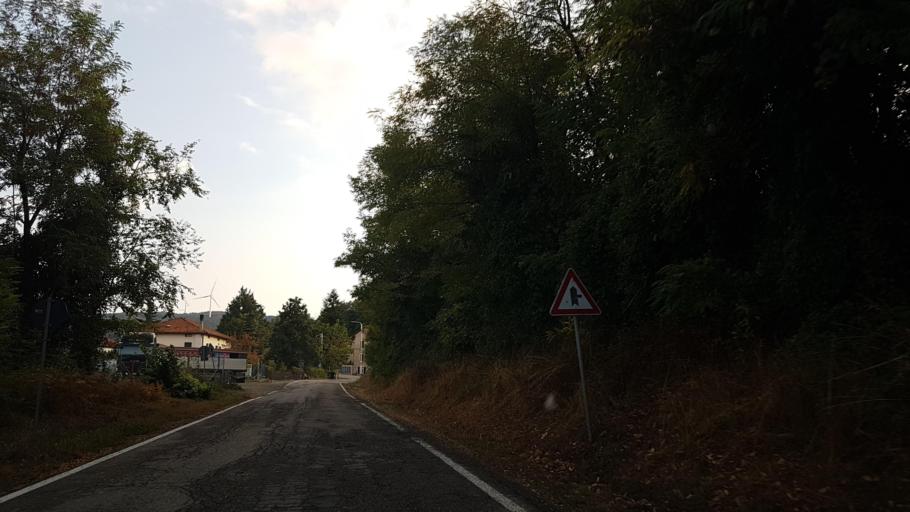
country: IT
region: Emilia-Romagna
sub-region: Provincia di Parma
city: Tornolo
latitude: 44.4397
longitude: 9.6353
